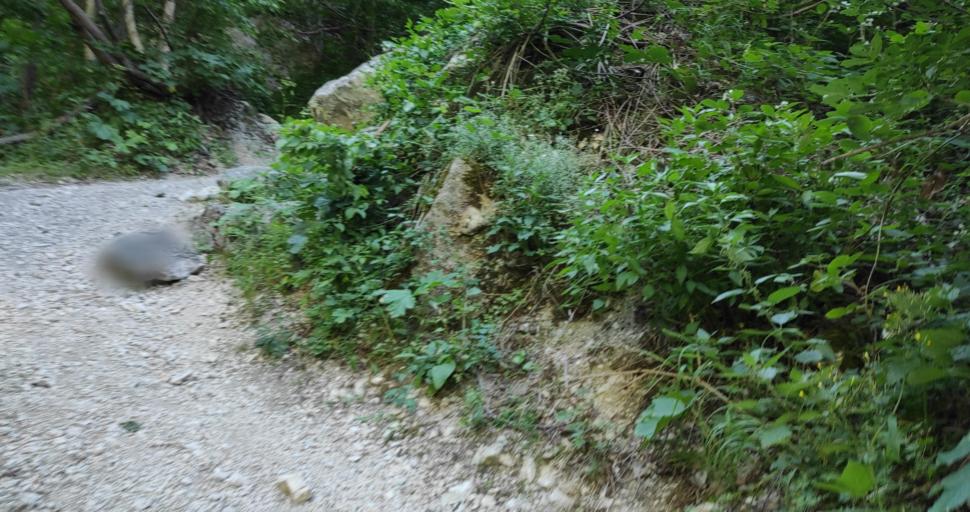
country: IT
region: The Marches
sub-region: Provincia di Ascoli Piceno
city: Montemonaco
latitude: 42.9209
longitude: 13.2790
